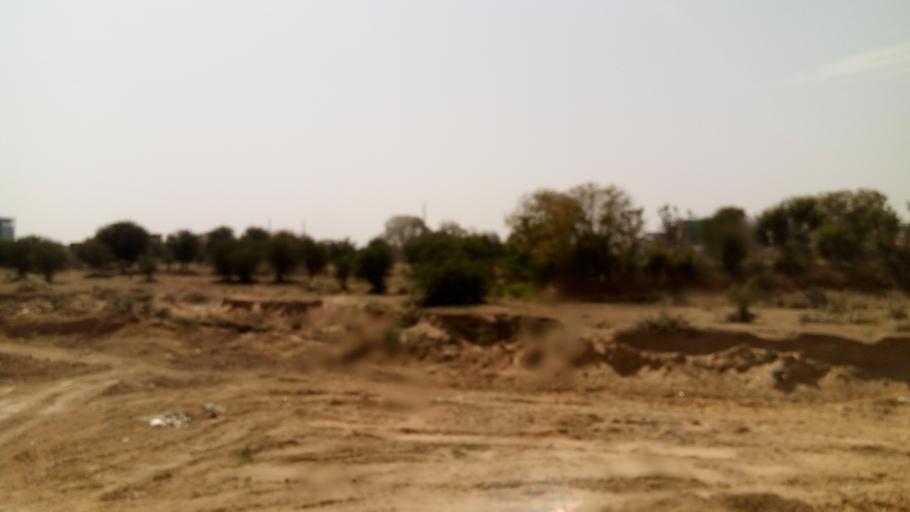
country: IN
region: Rajasthan
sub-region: Jaipur
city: Jaipur
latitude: 26.7951
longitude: 75.8170
